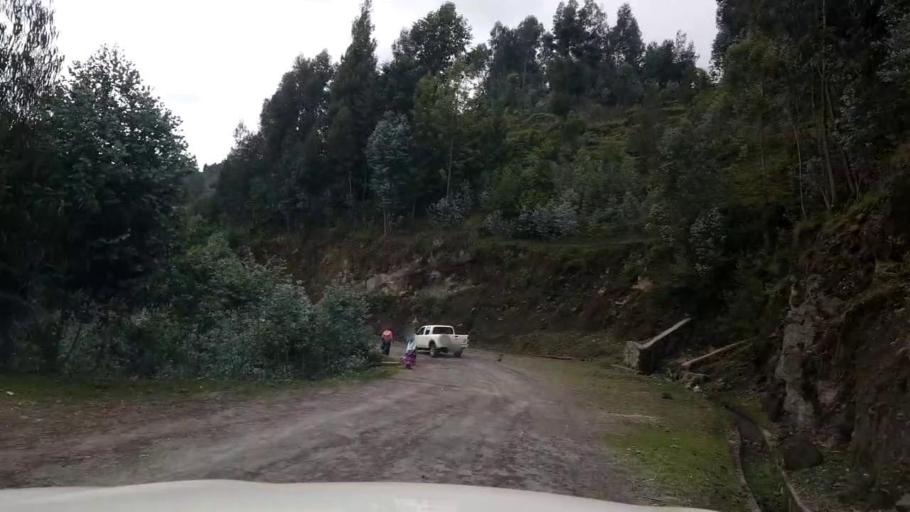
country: RW
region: Northern Province
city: Musanze
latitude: -1.5057
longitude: 29.5329
